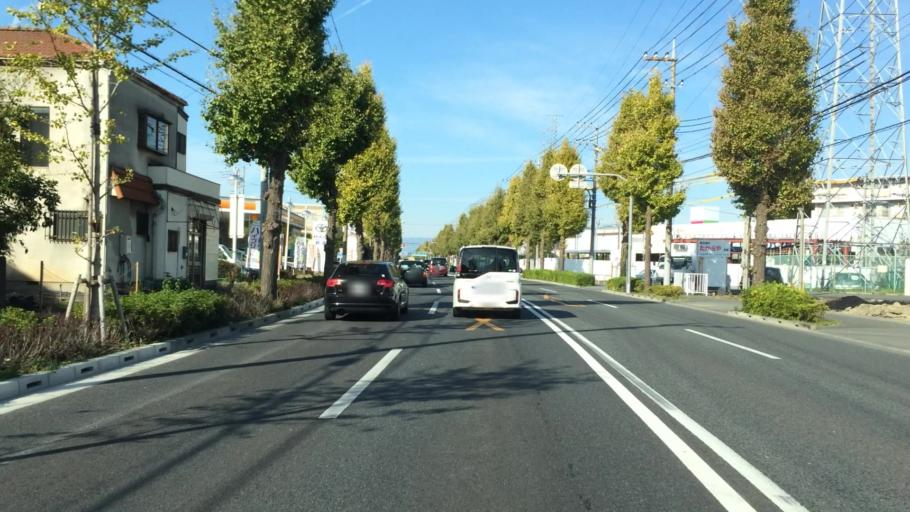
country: JP
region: Tokyo
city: Hino
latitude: 35.6904
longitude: 139.3990
